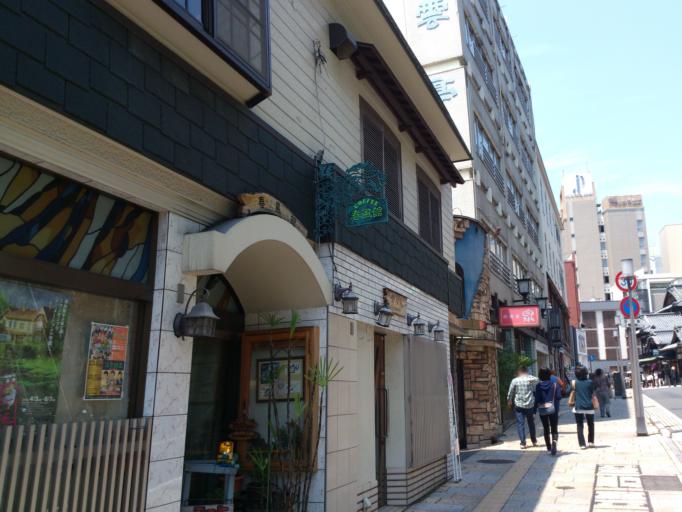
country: JP
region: Ehime
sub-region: Shikoku-chuo Shi
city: Matsuyama
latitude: 33.8512
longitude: 132.7859
